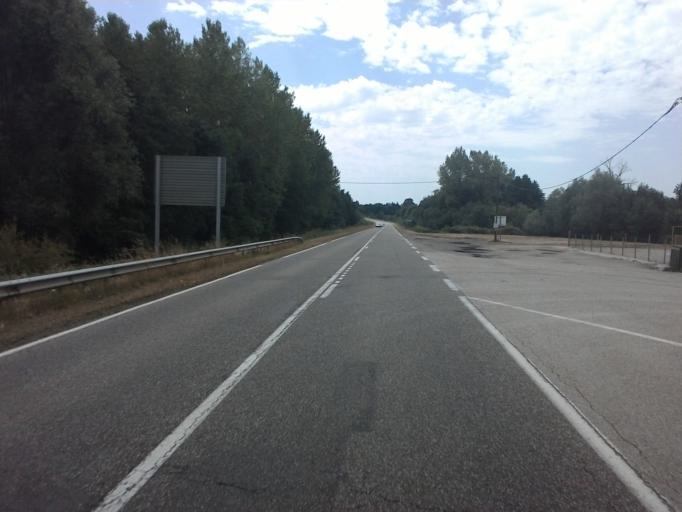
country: FR
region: Franche-Comte
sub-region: Departement du Jura
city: Saint-Amour
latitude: 46.4519
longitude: 5.3486
